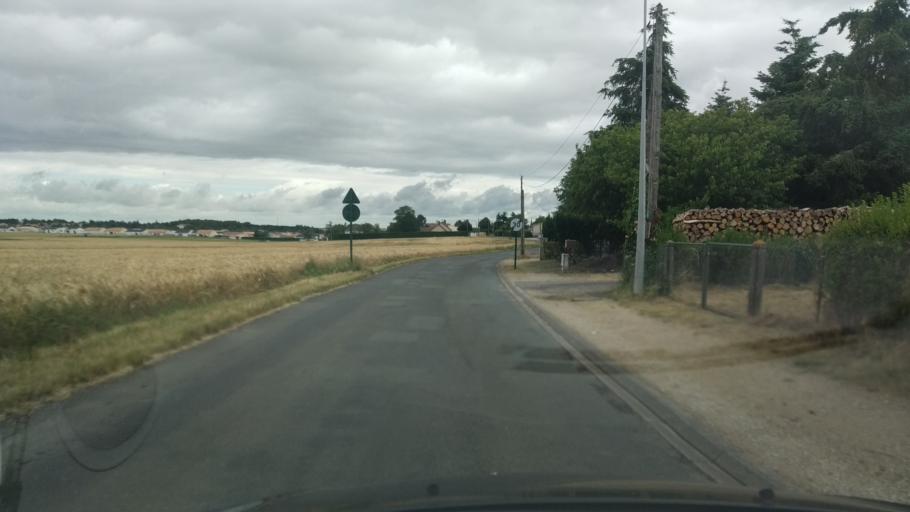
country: FR
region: Poitou-Charentes
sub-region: Departement de la Vienne
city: Vouneuil-sous-Biard
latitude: 46.5981
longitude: 0.2743
